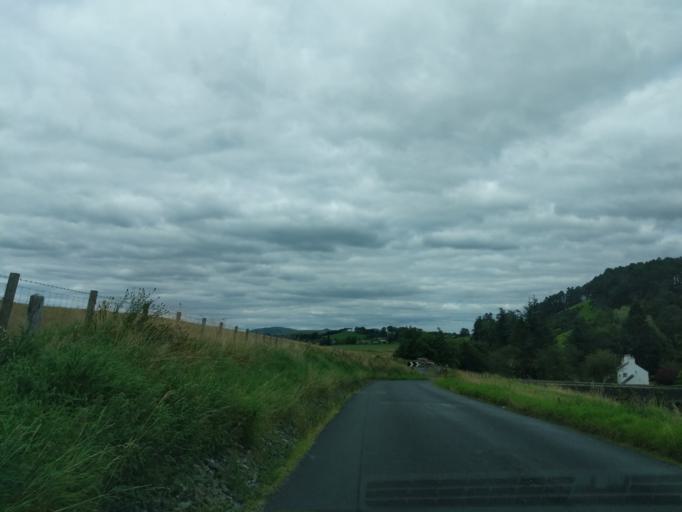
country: GB
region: Scotland
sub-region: The Scottish Borders
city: West Linton
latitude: 55.7051
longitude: -3.3385
